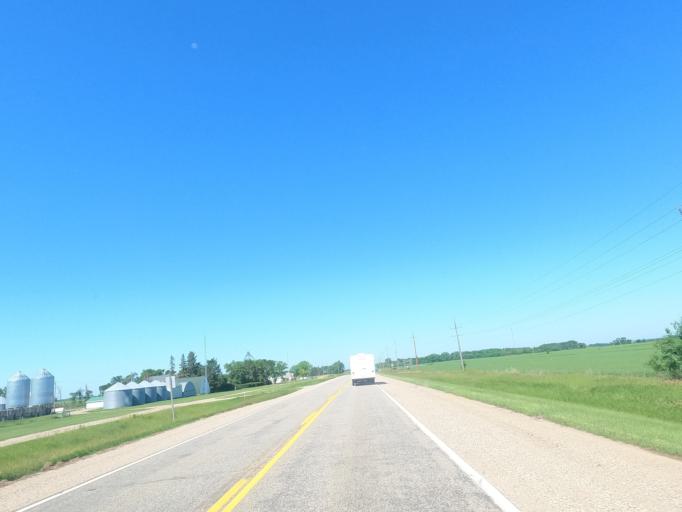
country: CA
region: Manitoba
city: Brandon
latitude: 49.5771
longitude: -99.6682
